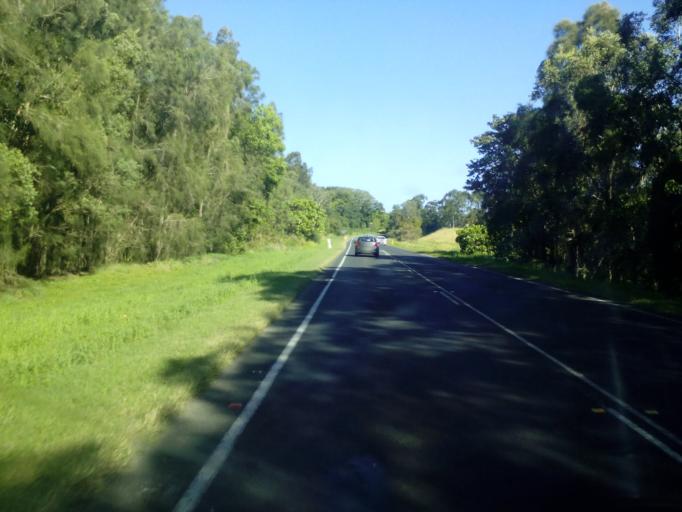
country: AU
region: New South Wales
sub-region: Tweed
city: Kingscliff
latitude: -28.2586
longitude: 153.5603
